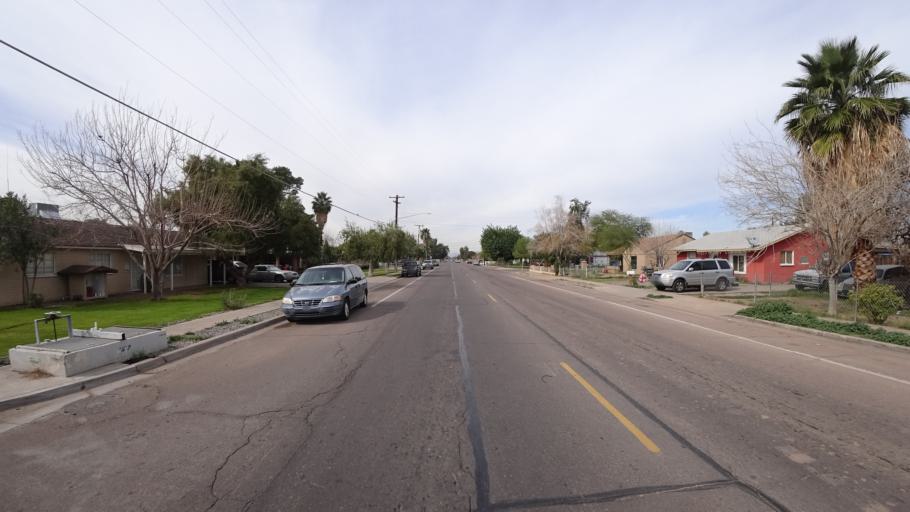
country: US
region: Arizona
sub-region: Maricopa County
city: Glendale
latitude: 33.5313
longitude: -112.1887
